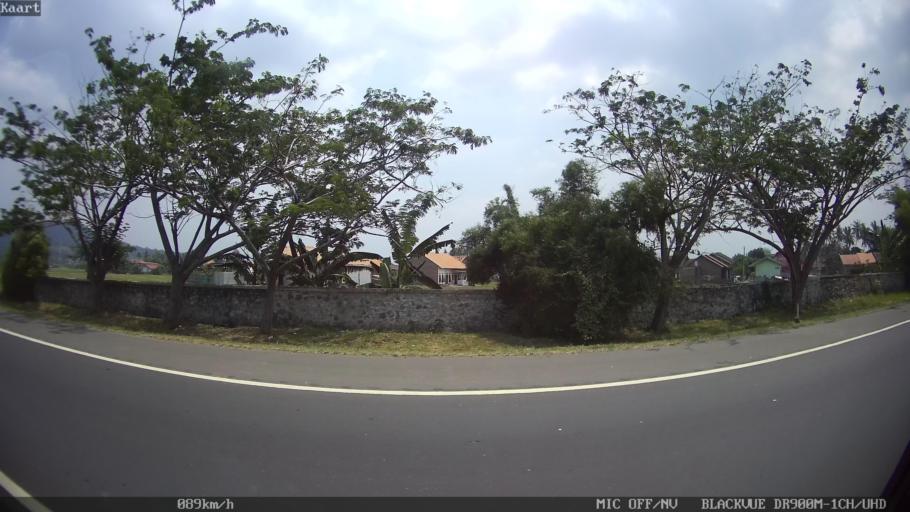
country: ID
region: Banten
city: Bojonegara
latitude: -6.0367
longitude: 106.1027
